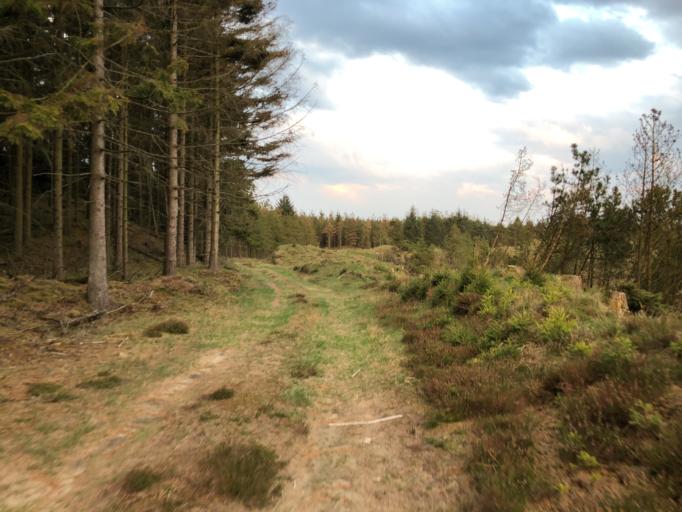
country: DK
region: Central Jutland
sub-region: Holstebro Kommune
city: Ulfborg
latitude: 56.2285
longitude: 8.4260
